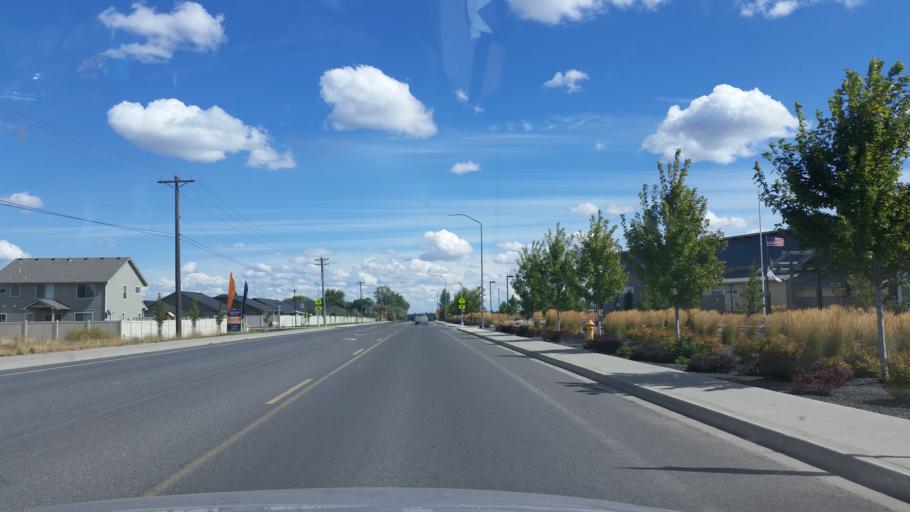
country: US
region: Washington
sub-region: Spokane County
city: Cheney
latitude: 47.5073
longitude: -117.5804
